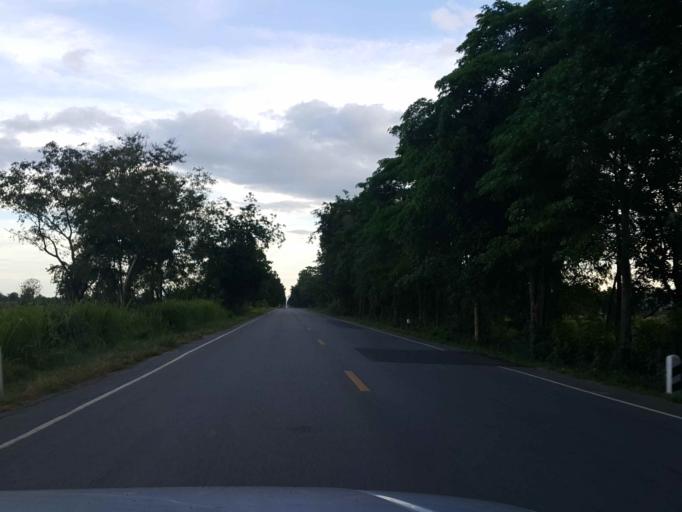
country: TH
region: Sukhothai
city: Sawankhalok
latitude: 17.3235
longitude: 99.7374
